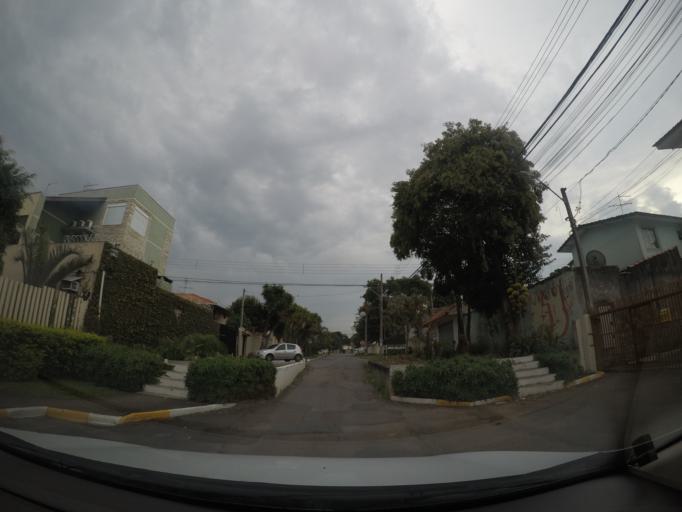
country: BR
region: Parana
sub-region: Sao Jose Dos Pinhais
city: Sao Jose dos Pinhais
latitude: -25.5217
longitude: -49.2352
